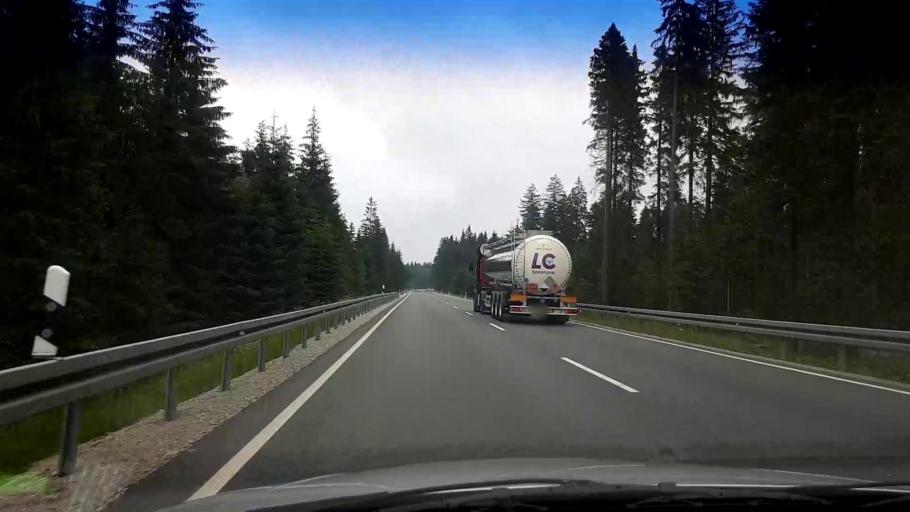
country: DE
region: Bavaria
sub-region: Upper Franconia
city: Fichtelberg
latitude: 50.0365
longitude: 11.8417
